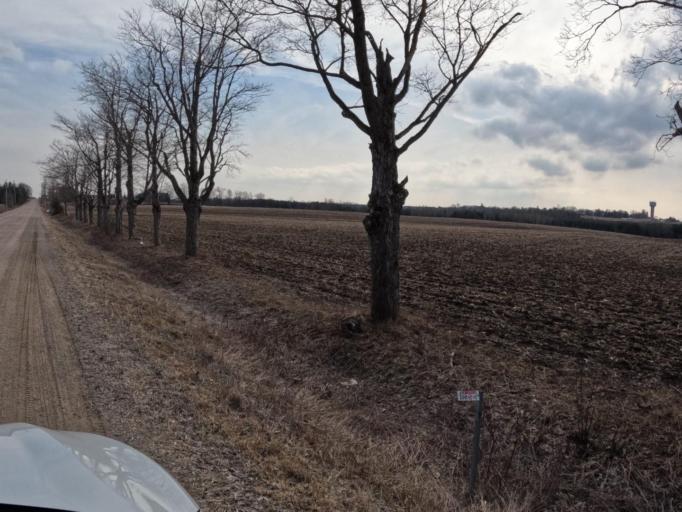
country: CA
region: Ontario
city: Shelburne
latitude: 43.9101
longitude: -80.3036
